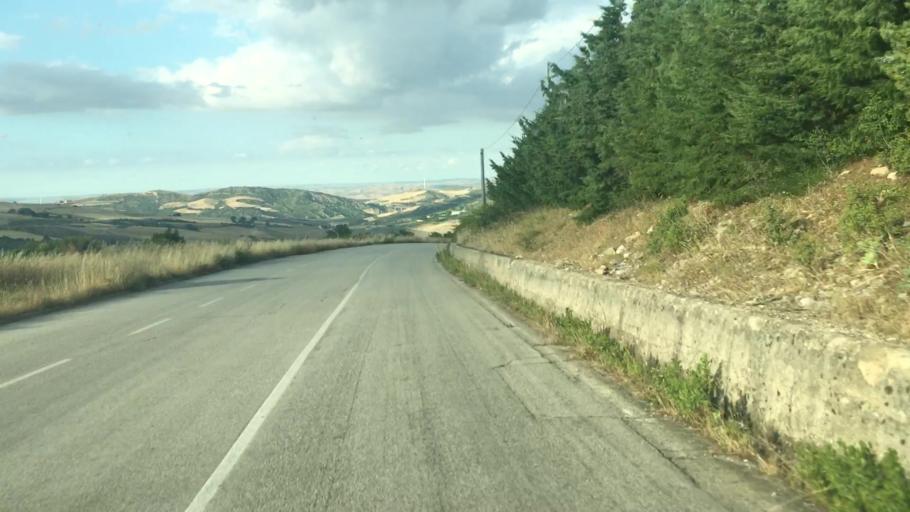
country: IT
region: Basilicate
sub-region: Provincia di Potenza
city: Tolve
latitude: 40.6982
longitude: 15.9956
